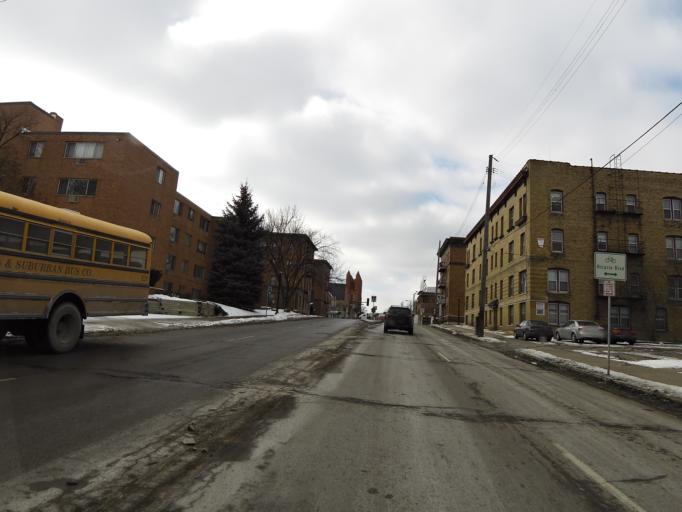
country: US
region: Minnesota
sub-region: Hennepin County
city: Minneapolis
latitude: 44.9627
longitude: -93.2896
